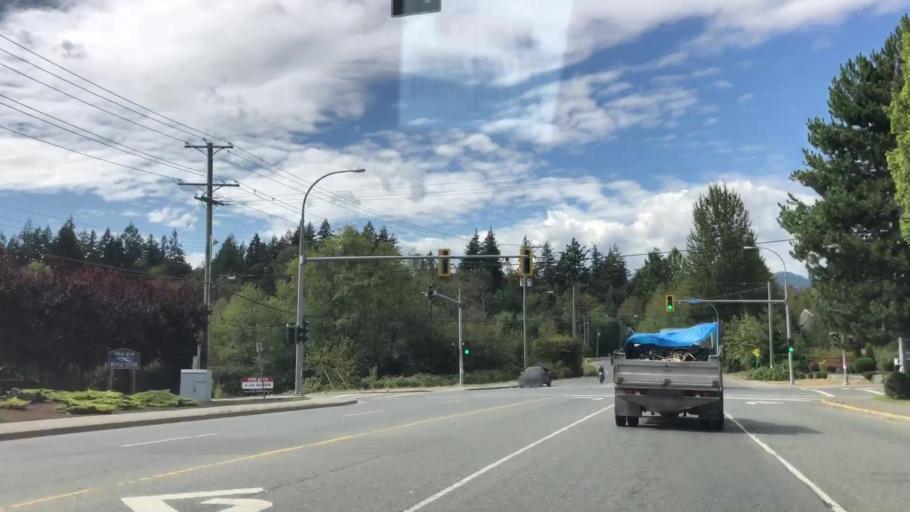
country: CA
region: British Columbia
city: Nanaimo
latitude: 49.1309
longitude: -123.9232
